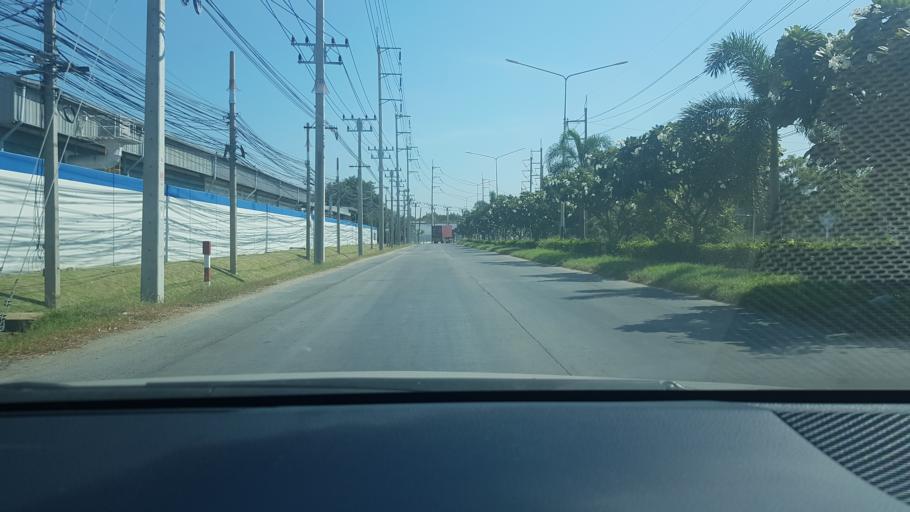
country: TH
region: Phra Nakhon Si Ayutthaya
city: Bang Pa-in
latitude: 14.2518
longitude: 100.6054
